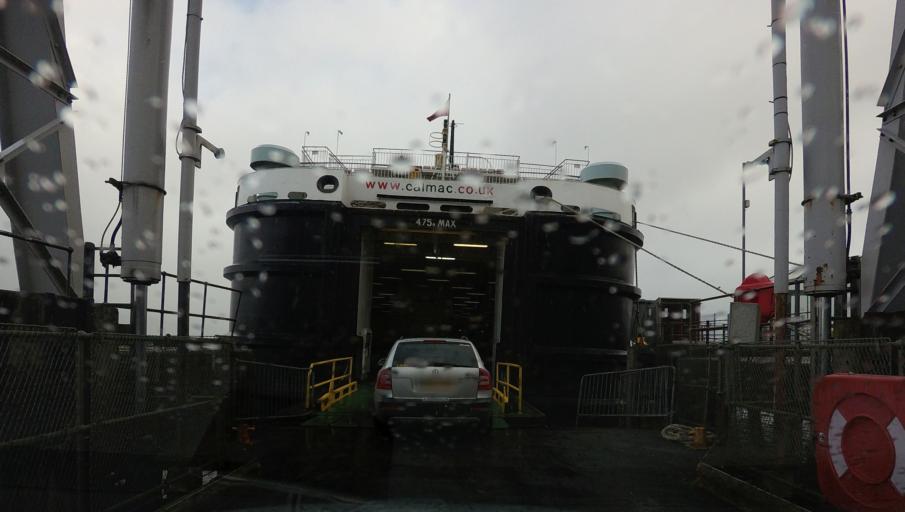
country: GB
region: Scotland
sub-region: Argyll and Bute
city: Isle Of Mull
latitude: 56.4712
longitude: -5.7058
